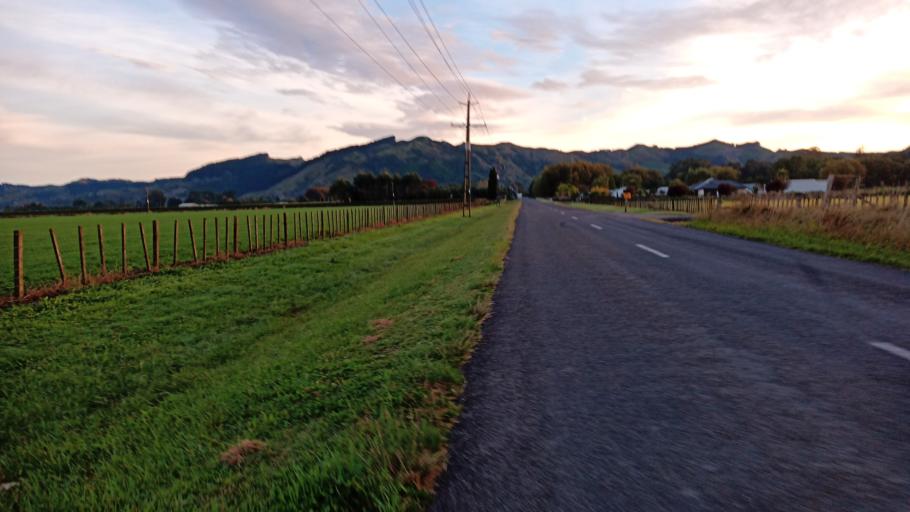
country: NZ
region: Gisborne
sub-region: Gisborne District
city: Gisborne
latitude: -38.6260
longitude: 177.9775
